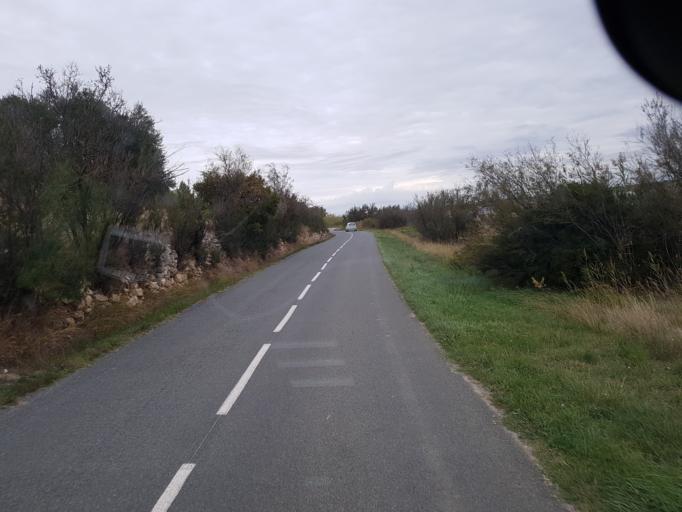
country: FR
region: Languedoc-Roussillon
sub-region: Departement de l'Aude
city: Peyriac-de-Mer
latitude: 43.1312
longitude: 2.9854
